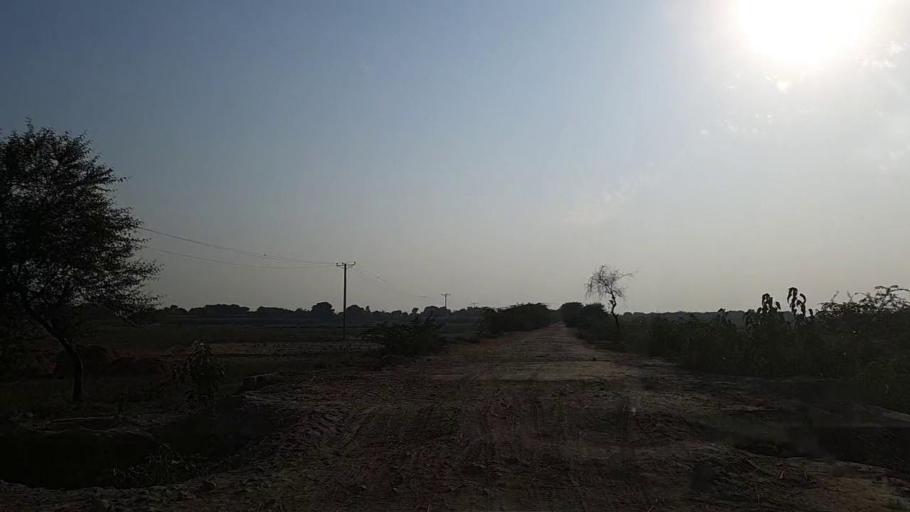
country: PK
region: Sindh
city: Mirpur Batoro
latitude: 24.7872
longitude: 68.2487
